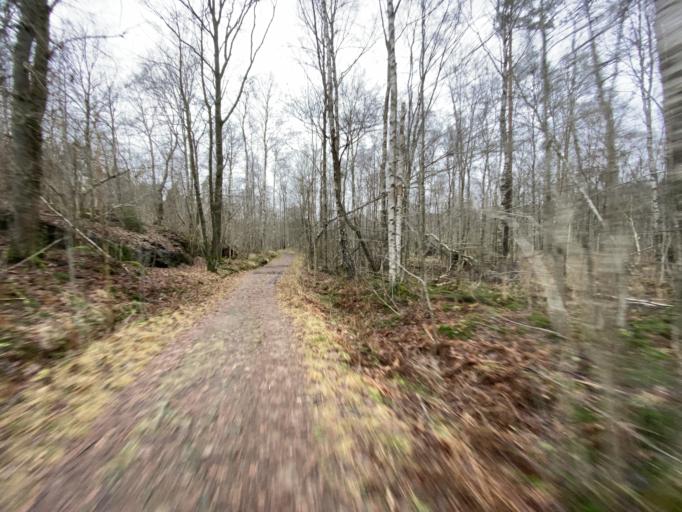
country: SE
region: Vaestra Goetaland
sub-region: Molndal
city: Moelndal
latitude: 57.7057
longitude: 12.0353
